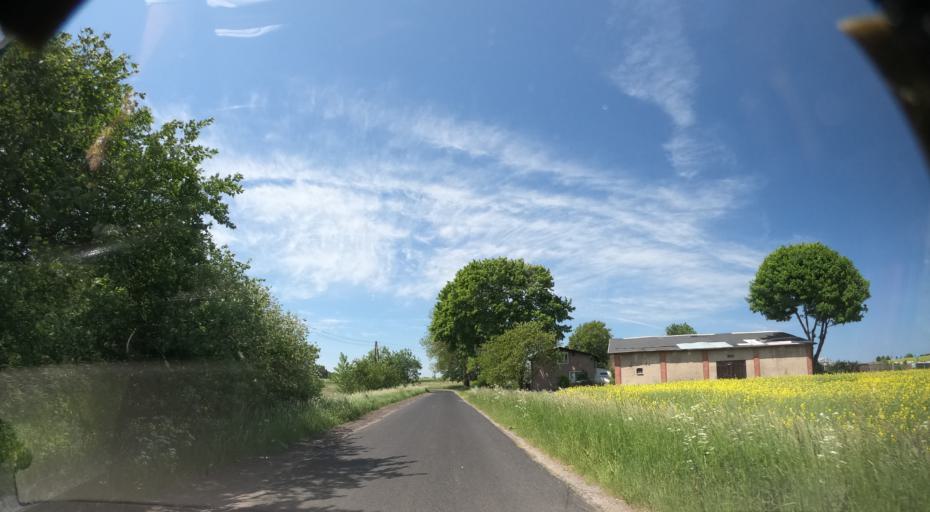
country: PL
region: West Pomeranian Voivodeship
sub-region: Powiat kolobrzeski
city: Dygowo
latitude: 54.1428
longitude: 15.7342
